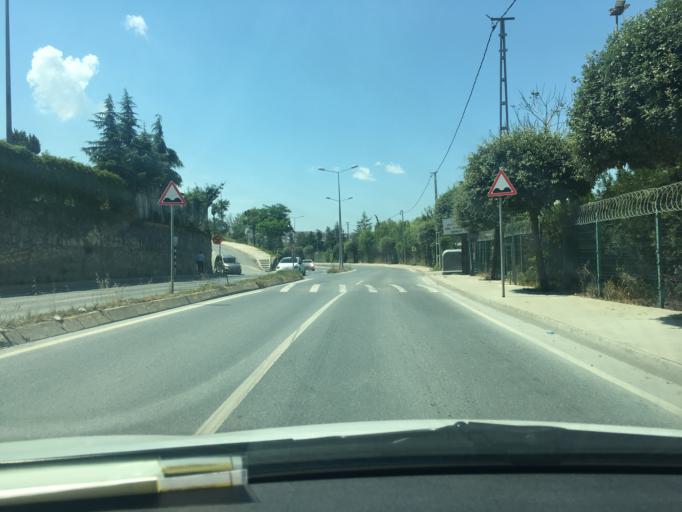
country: TR
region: Istanbul
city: Sisli
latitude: 41.0897
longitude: 28.9318
